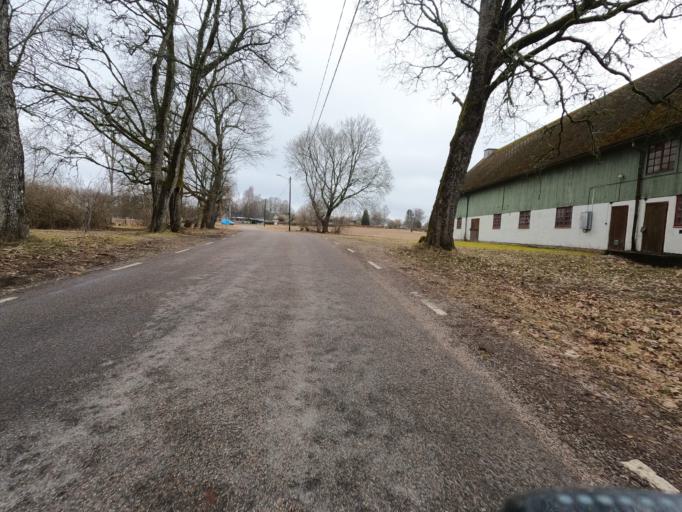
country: SE
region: Kronoberg
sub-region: Ljungby Kommun
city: Ljungby
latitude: 56.8272
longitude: 13.7561
